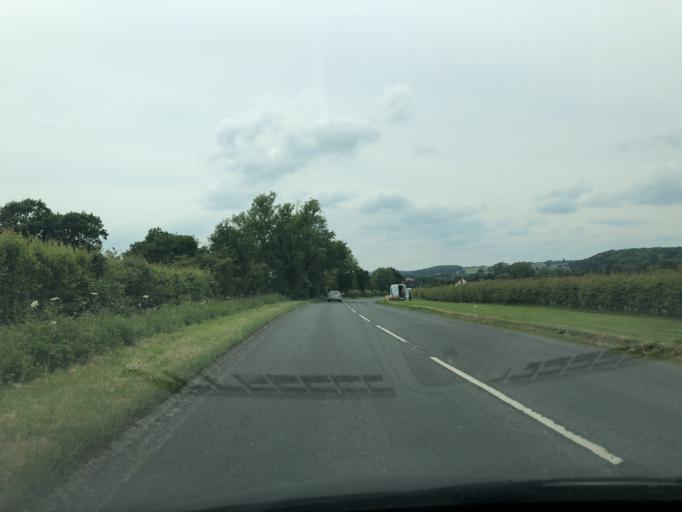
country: GB
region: England
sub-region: North Yorkshire
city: Great Habton
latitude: 54.2639
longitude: -0.9032
